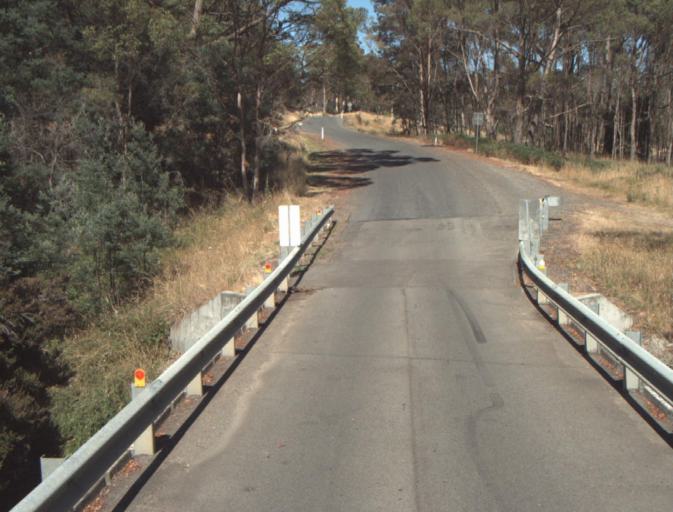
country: AU
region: Tasmania
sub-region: Launceston
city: Newstead
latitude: -41.3658
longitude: 147.3050
